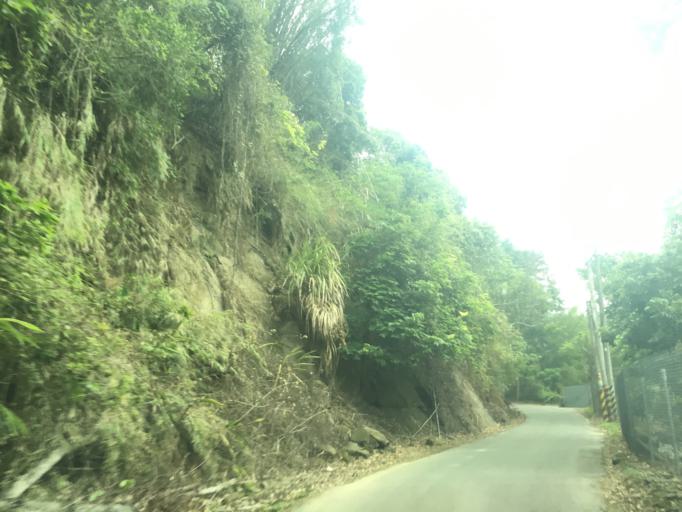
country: TW
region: Taiwan
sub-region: Taichung City
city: Taichung
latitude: 24.0607
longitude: 120.7692
